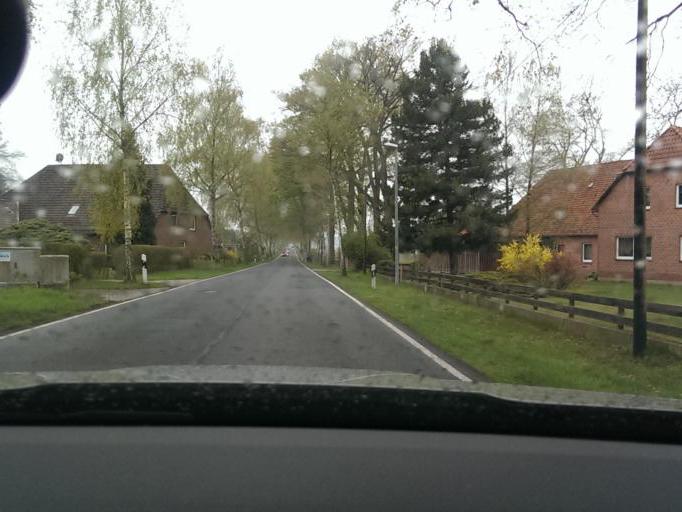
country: DE
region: Lower Saxony
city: Steimbke
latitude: 52.6107
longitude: 9.4779
